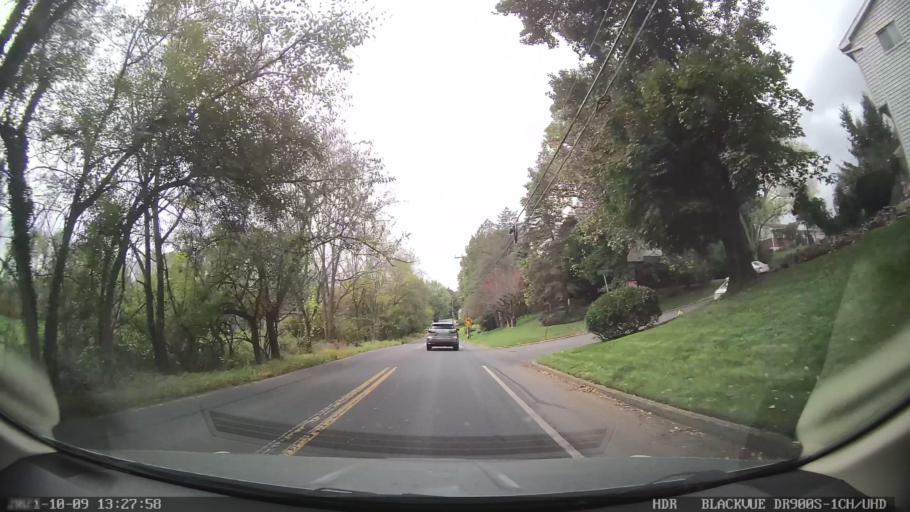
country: US
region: Pennsylvania
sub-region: Lehigh County
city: Ancient Oaks
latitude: 40.5420
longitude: -75.5892
